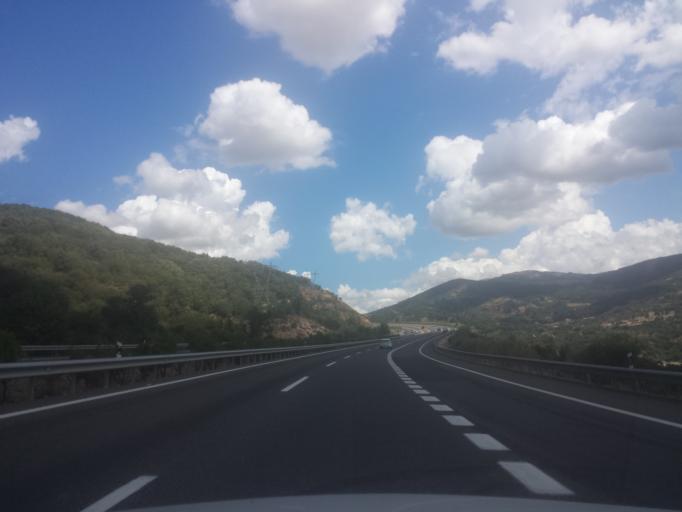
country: ES
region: Extremadura
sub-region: Provincia de Caceres
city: Banos de Montemayor
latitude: 40.3019
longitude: -5.8862
